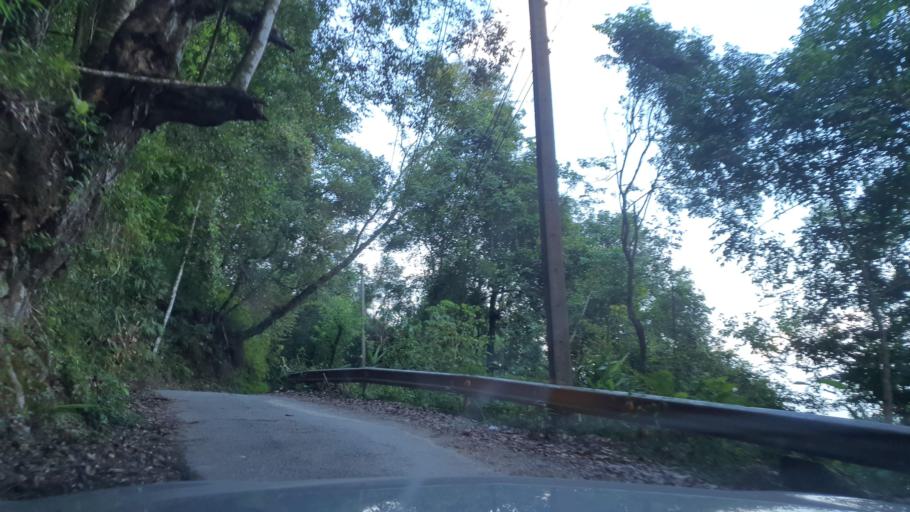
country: TH
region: Chiang Mai
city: Chiang Mai
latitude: 18.8285
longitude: 98.8986
